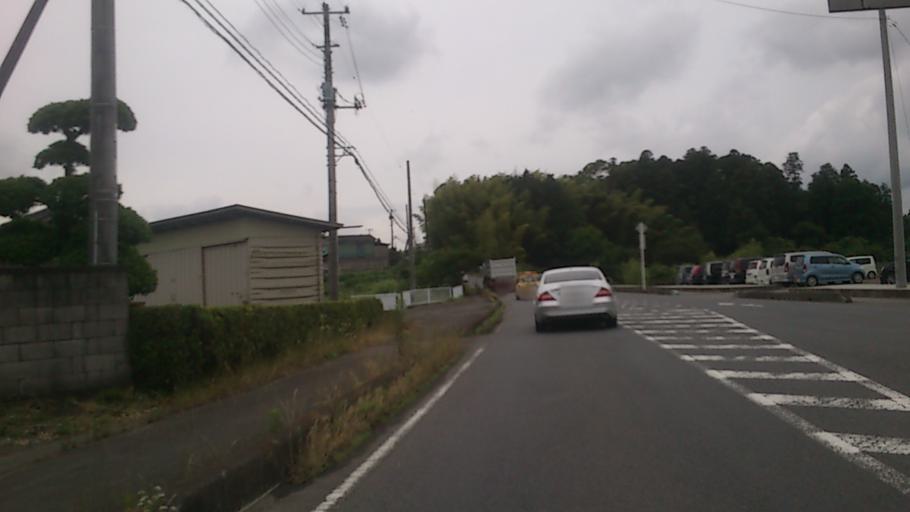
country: JP
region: Ibaraki
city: Okunoya
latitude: 36.2906
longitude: 140.3824
